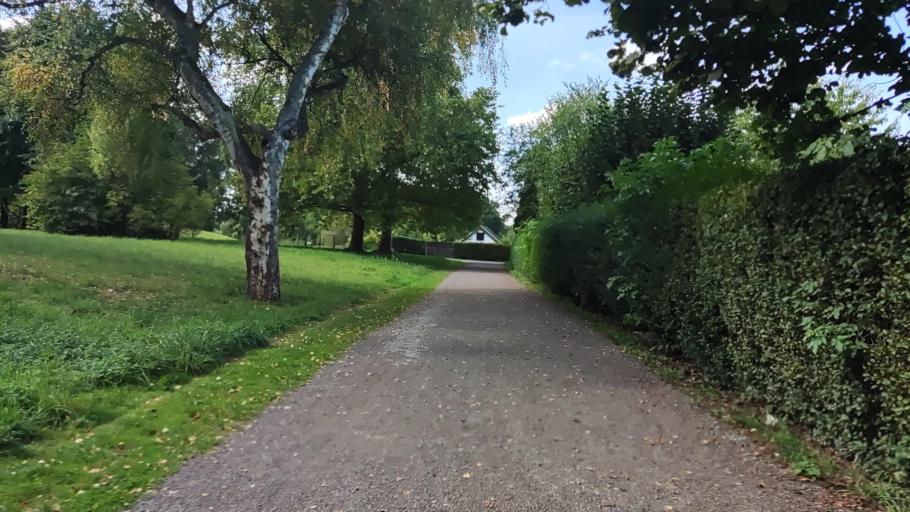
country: DE
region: North Rhine-Westphalia
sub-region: Regierungsbezirk Arnsberg
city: Bochum
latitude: 51.4702
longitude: 7.2351
